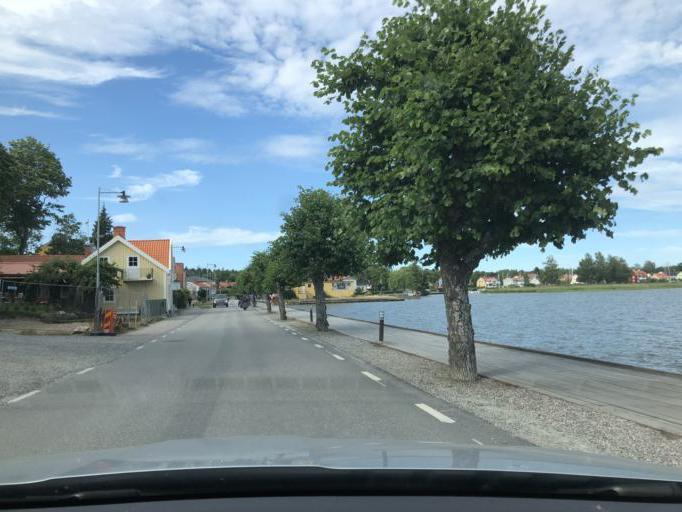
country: SE
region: Soedermanland
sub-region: Strangnas Kommun
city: Mariefred
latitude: 59.2578
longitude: 17.2249
